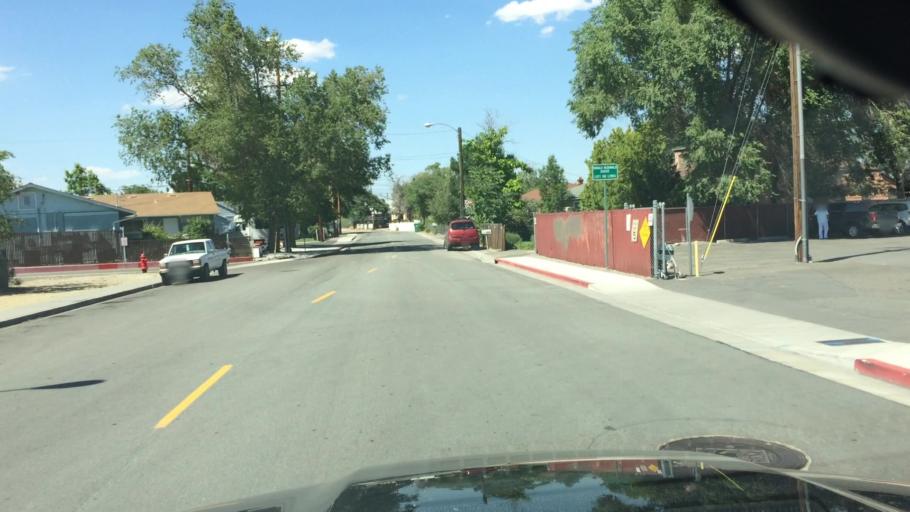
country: US
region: Nevada
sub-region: Washoe County
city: Reno
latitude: 39.5245
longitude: -119.7912
